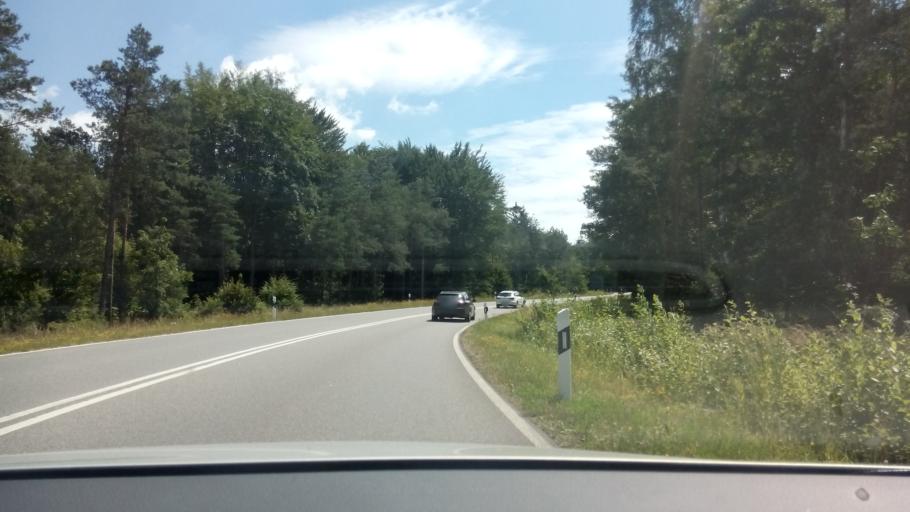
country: DE
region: Bavaria
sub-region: Upper Bavaria
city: Oberschleissheim
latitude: 48.2520
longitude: 11.5805
